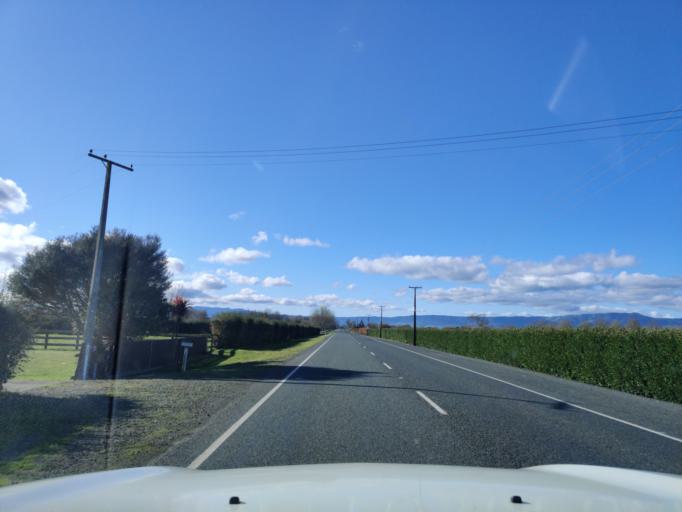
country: NZ
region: Waikato
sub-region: Matamata-Piako District
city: Matamata
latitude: -37.8737
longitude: 175.7430
